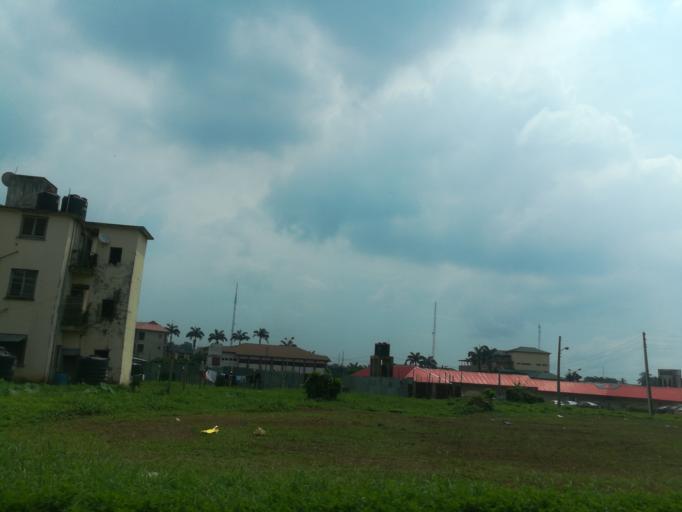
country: NG
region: Oyo
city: Ibadan
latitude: 7.4008
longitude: 3.9087
